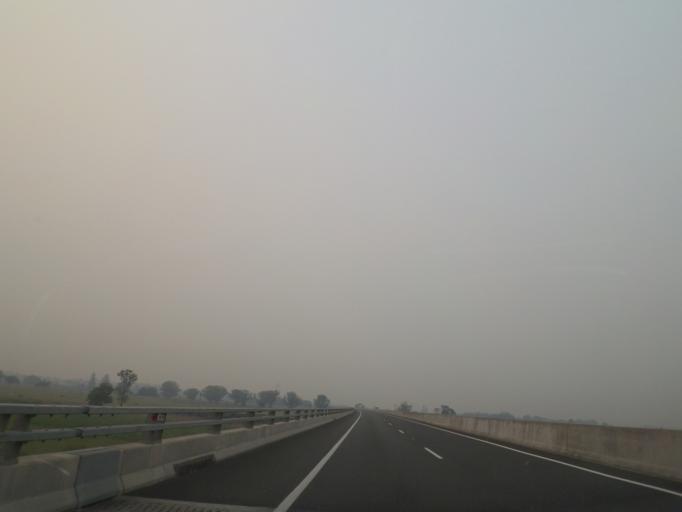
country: AU
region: New South Wales
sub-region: Kempsey
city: Frederickton
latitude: -31.0453
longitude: 152.8886
